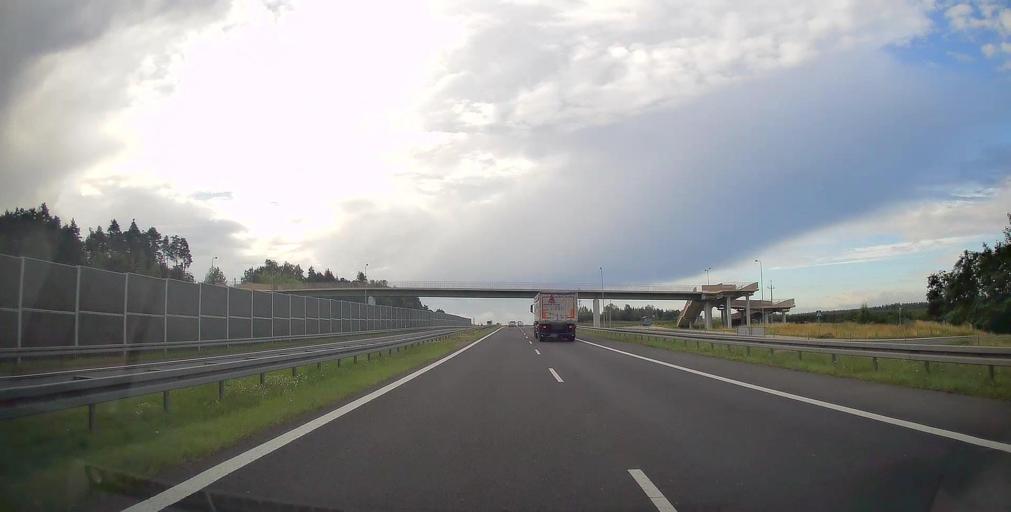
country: PL
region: Masovian Voivodeship
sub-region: Powiat bialobrzeski
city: Promna
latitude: 51.7239
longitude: 20.9196
